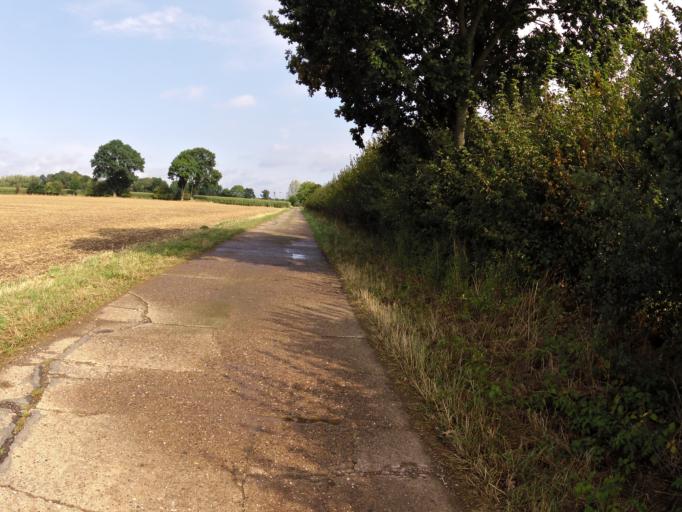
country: DE
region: Lower Saxony
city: Drakenburg
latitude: 52.7008
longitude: 9.1920
